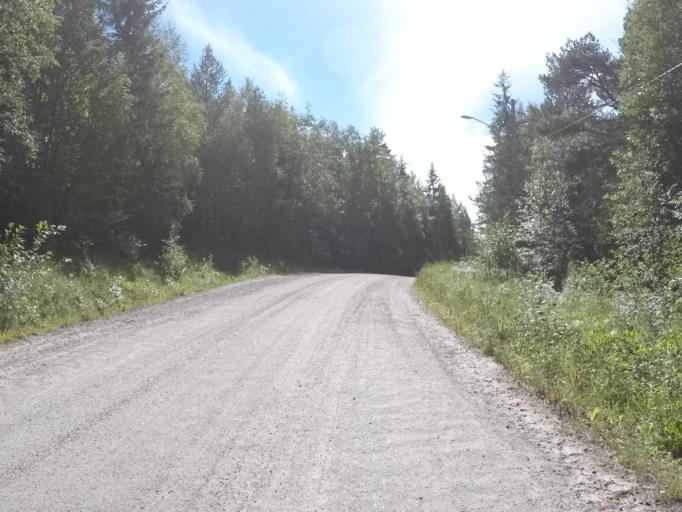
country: SE
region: Vaesterbotten
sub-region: Robertsfors Kommun
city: Robertsfors
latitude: 64.0054
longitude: 20.8137
